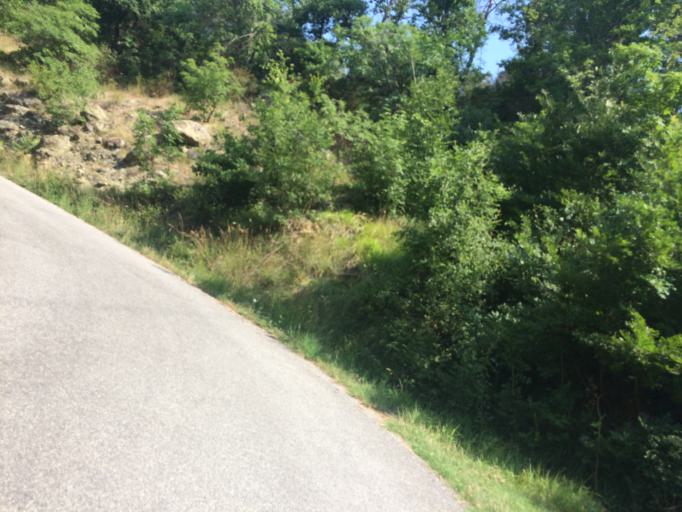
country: IT
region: Piedmont
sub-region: Provincia di Alessandria
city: Pareto
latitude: 44.4854
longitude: 8.3520
